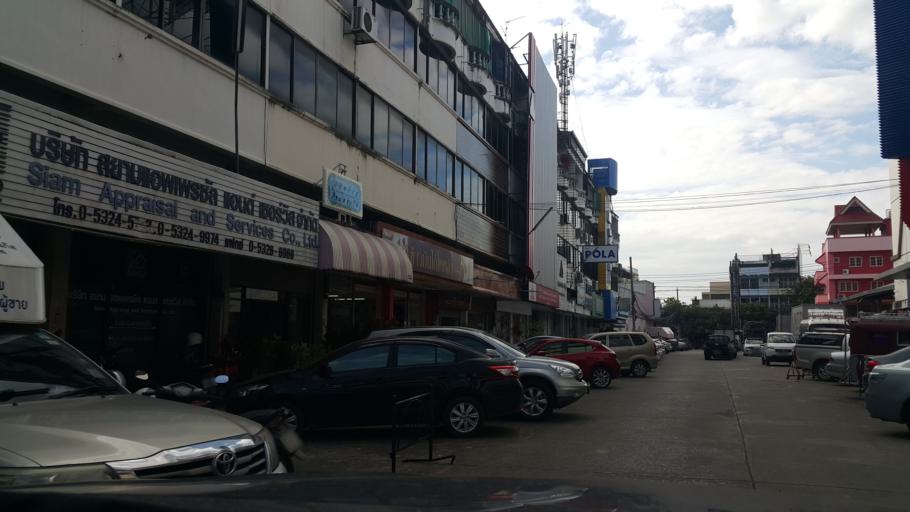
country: TH
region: Chiang Mai
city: Chiang Mai
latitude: 18.7870
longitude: 99.0147
